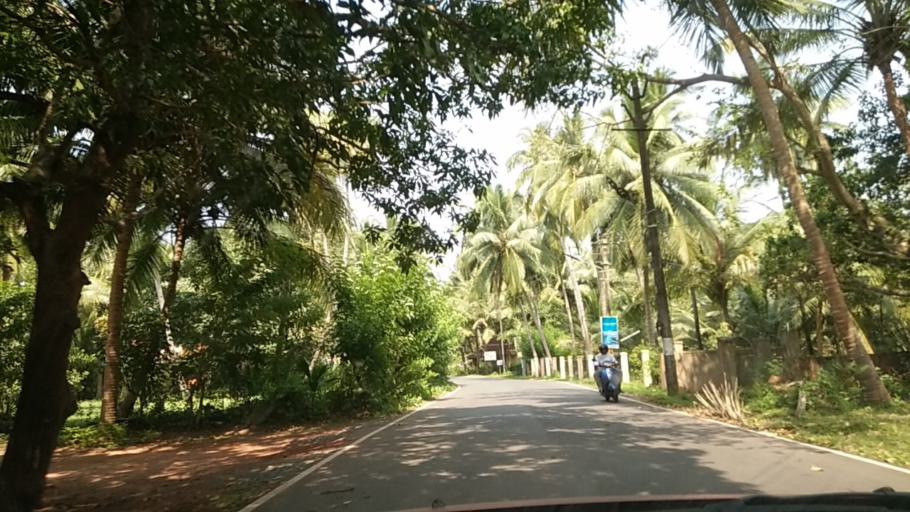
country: IN
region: Goa
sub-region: South Goa
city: Colva
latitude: 15.3248
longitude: 73.9049
